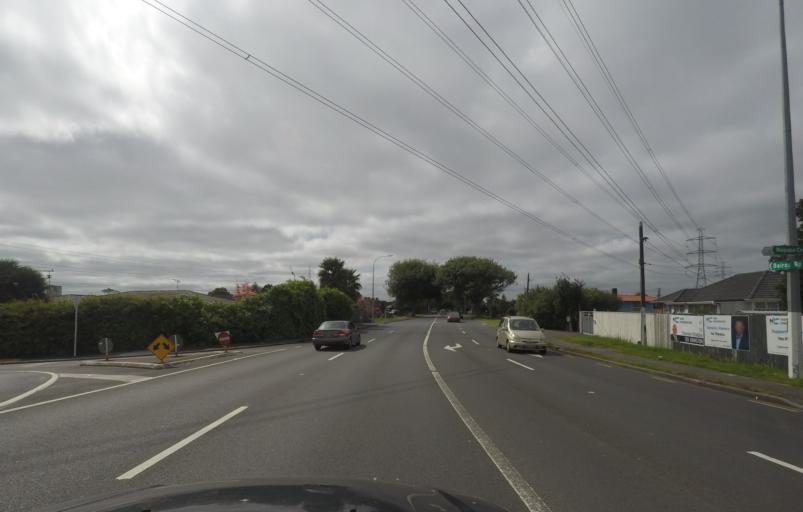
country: NZ
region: Auckland
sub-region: Auckland
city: Manukau City
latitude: -36.9569
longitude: 174.8630
